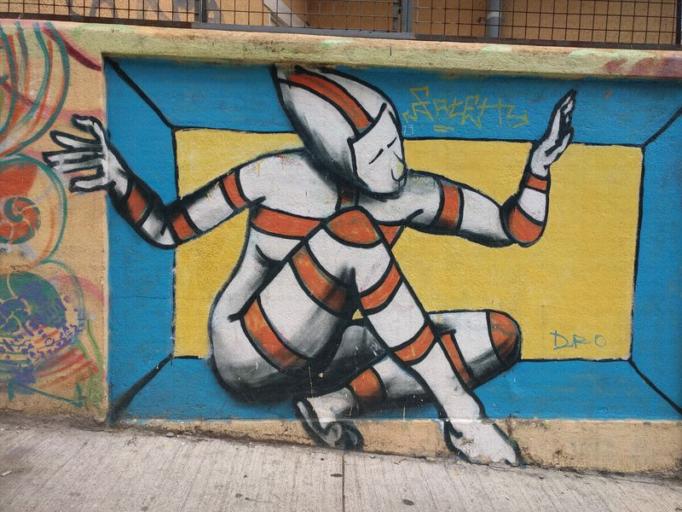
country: CL
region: Valparaiso
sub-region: Provincia de Valparaiso
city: Valparaiso
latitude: -33.0436
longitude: -71.6269
